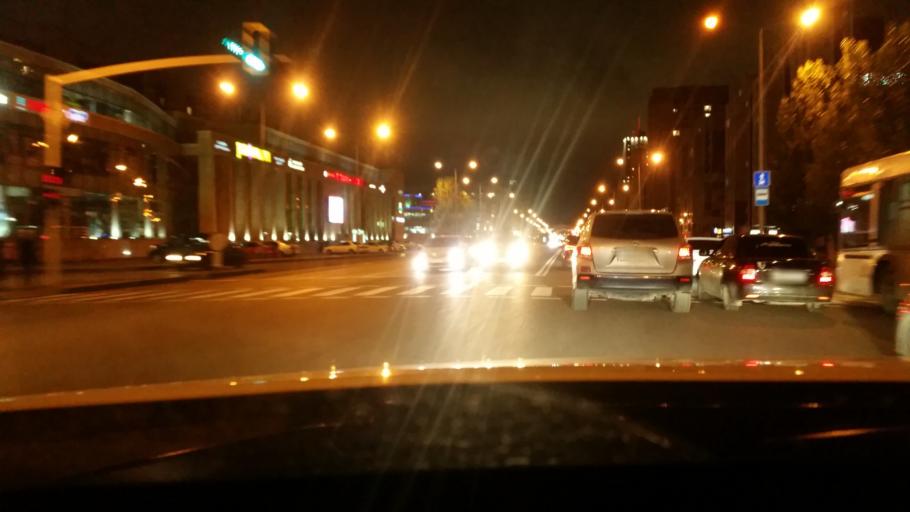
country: KZ
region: Astana Qalasy
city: Astana
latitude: 51.1397
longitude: 71.4770
